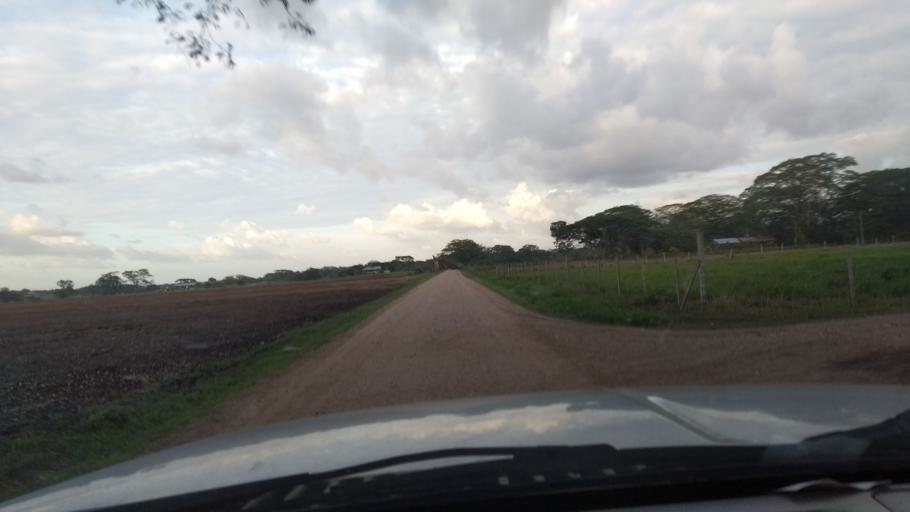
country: BZ
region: Cayo
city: San Ignacio
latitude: 17.2172
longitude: -89.0018
